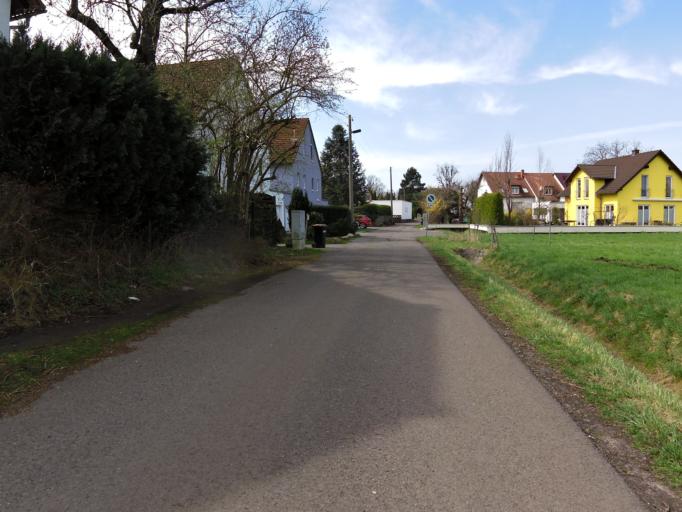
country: DE
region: Saxony
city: Schkeuditz
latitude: 51.3819
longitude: 12.2771
